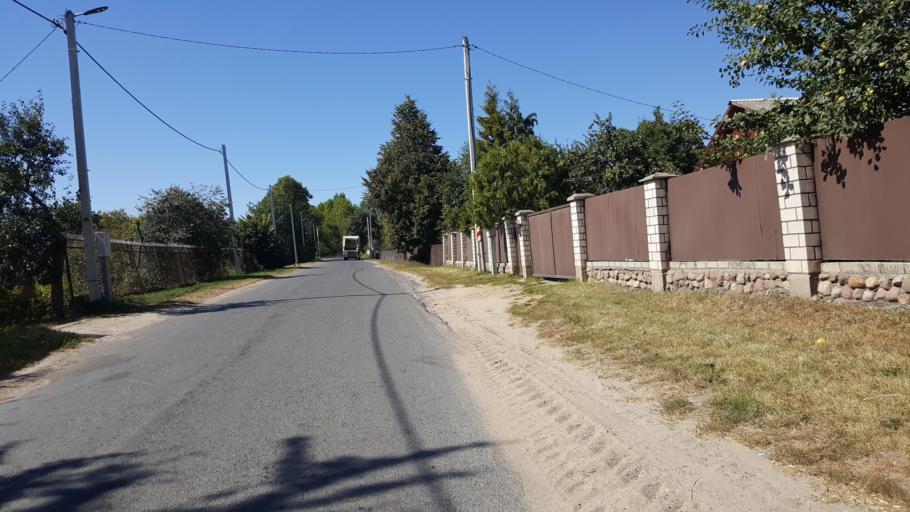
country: BY
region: Brest
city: Vysokaye
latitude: 52.2217
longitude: 23.4382
